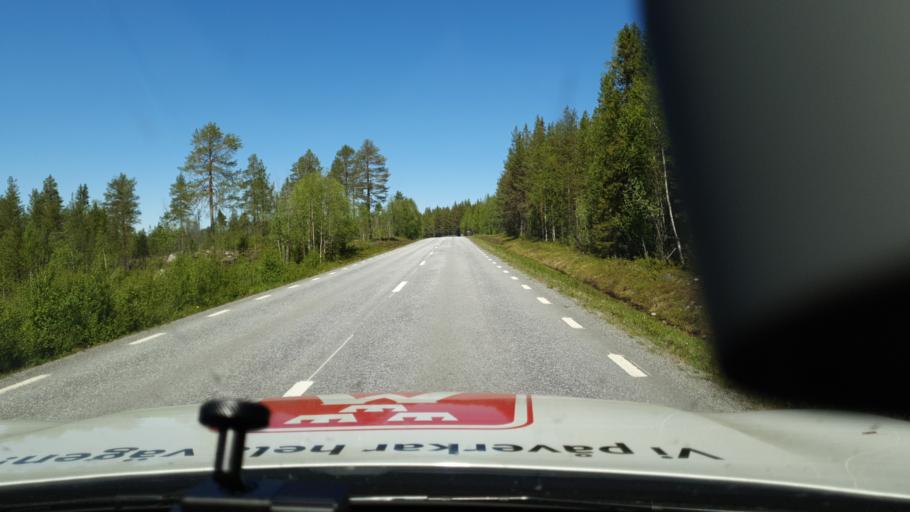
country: SE
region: Vaesterbotten
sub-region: Storumans Kommun
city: Storuman
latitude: 65.1350
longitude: 17.1056
